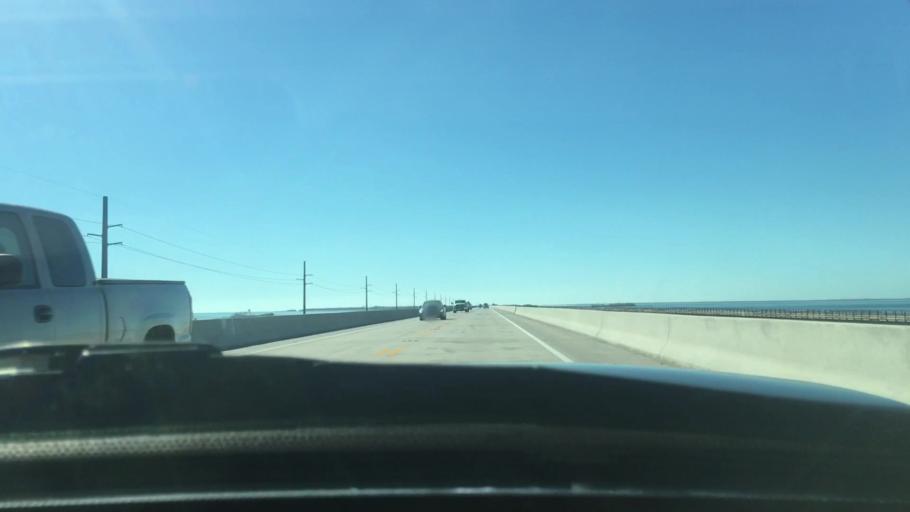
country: US
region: Florida
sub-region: Monroe County
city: Marathon
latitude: 24.6887
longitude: -81.2061
